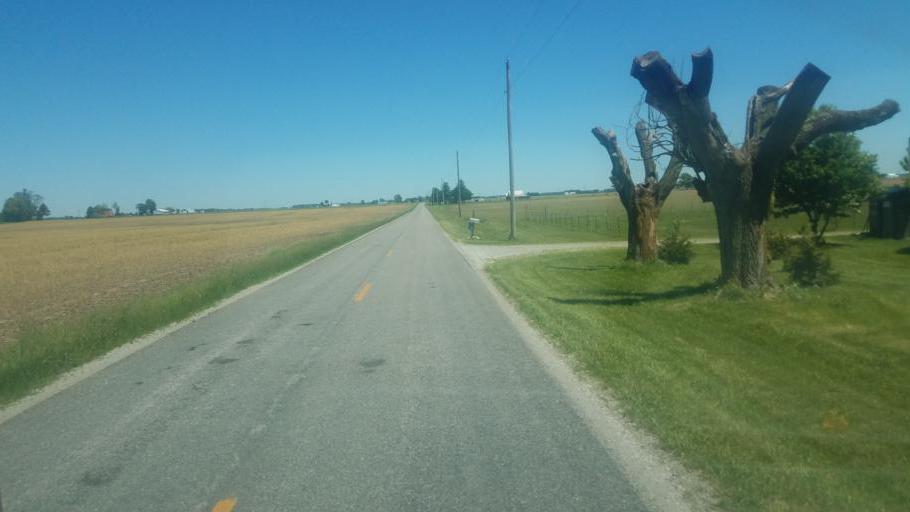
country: US
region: Ohio
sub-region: Shelby County
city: Sidney
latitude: 40.2116
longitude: -84.1234
